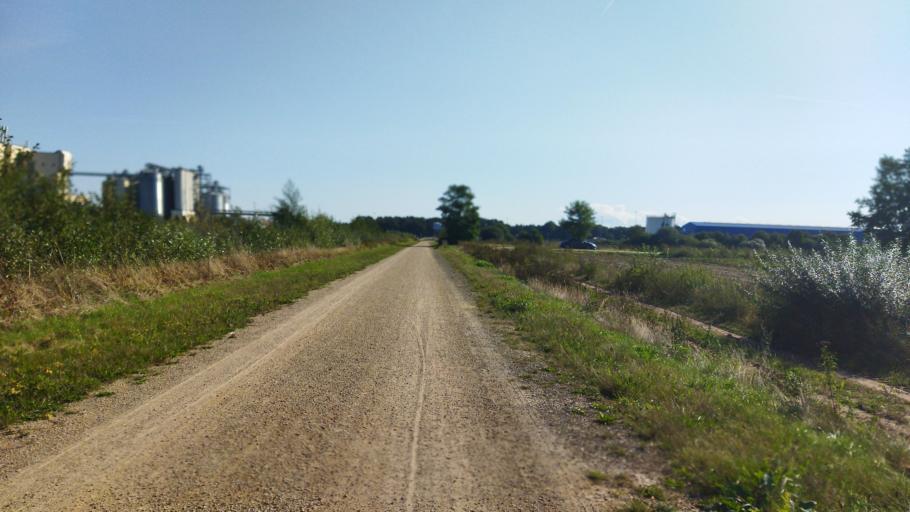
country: DE
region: Lower Saxony
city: Haren
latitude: 52.7769
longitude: 7.2669
